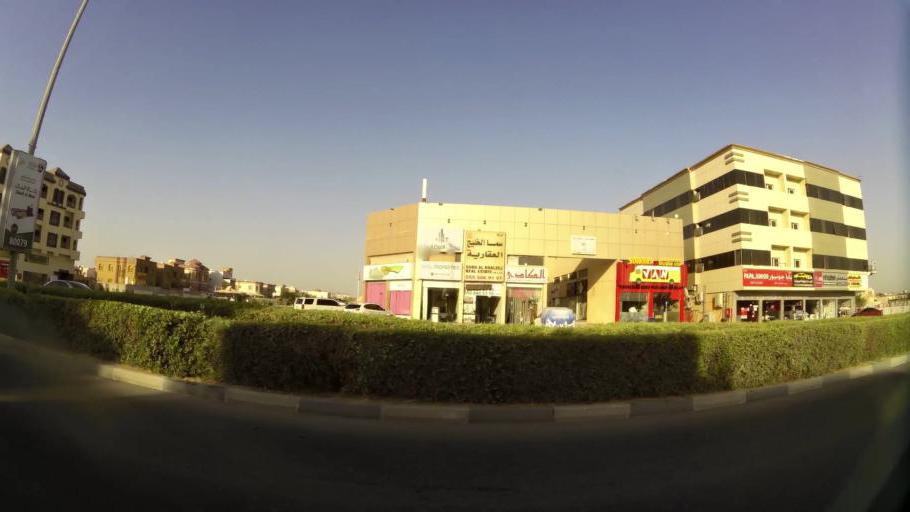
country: AE
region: Ajman
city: Ajman
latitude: 25.3868
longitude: 55.5063
